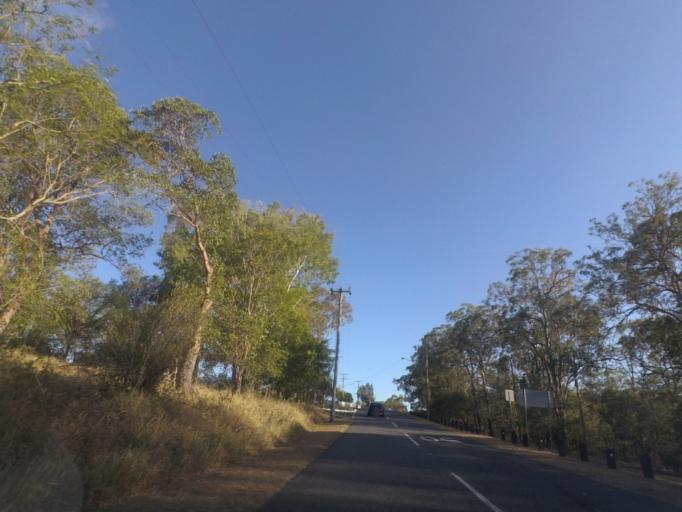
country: AU
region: Queensland
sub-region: Brisbane
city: Taringa
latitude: -27.4707
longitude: 152.9713
